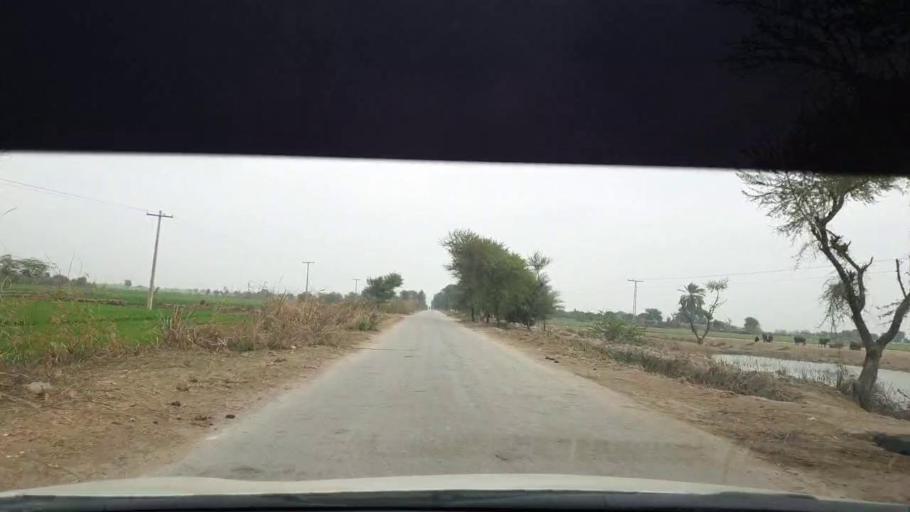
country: PK
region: Sindh
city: Berani
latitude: 25.7760
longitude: 68.8654
